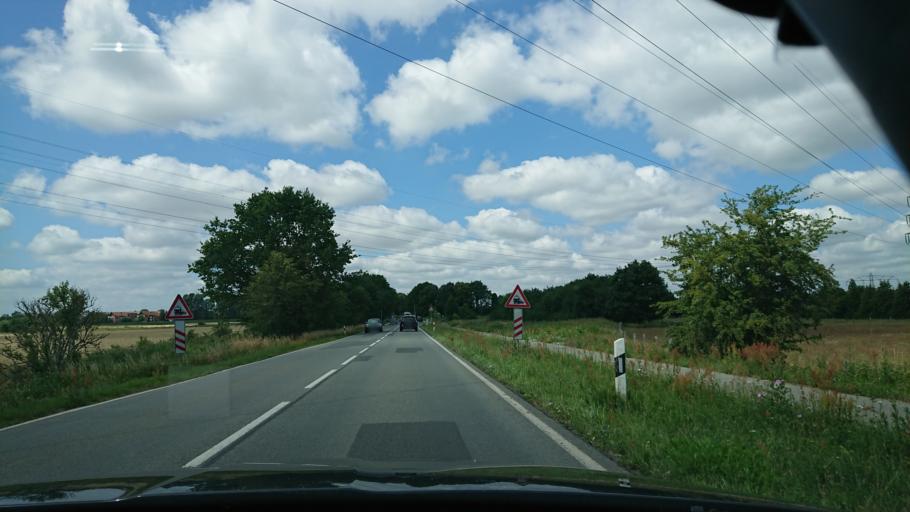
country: DE
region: Brandenburg
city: Perleberg
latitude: 53.0665
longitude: 11.8863
